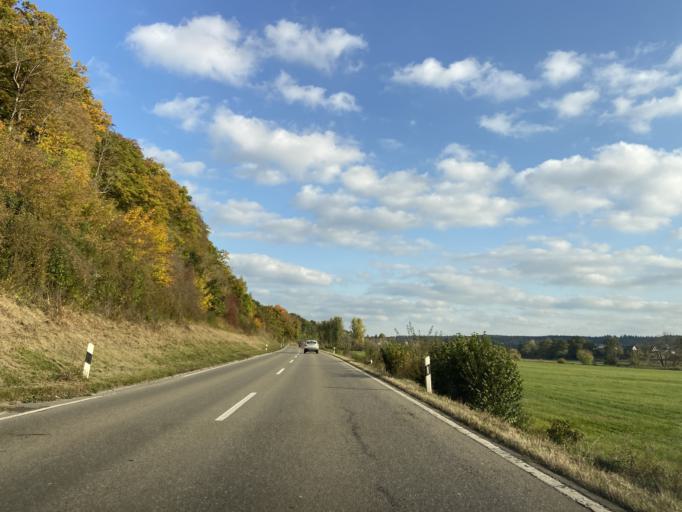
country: DE
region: Baden-Wuerttemberg
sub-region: Tuebingen Region
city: Sigmaringendorf
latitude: 48.0746
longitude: 9.2476
